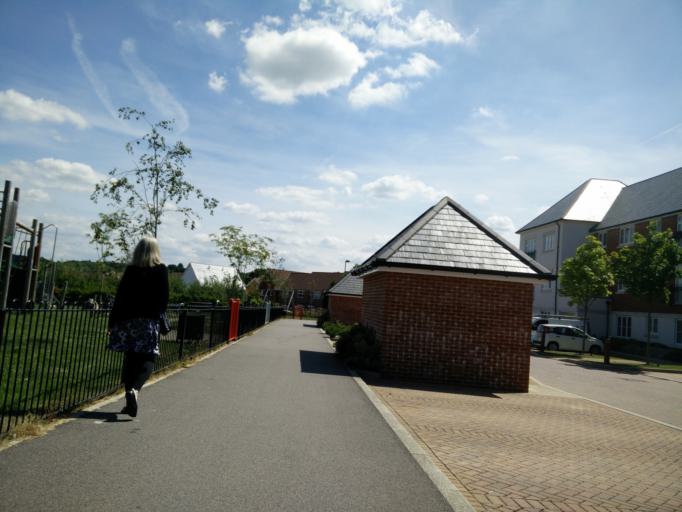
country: GB
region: England
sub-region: West Sussex
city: Horsham
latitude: 51.0642
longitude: -0.3542
